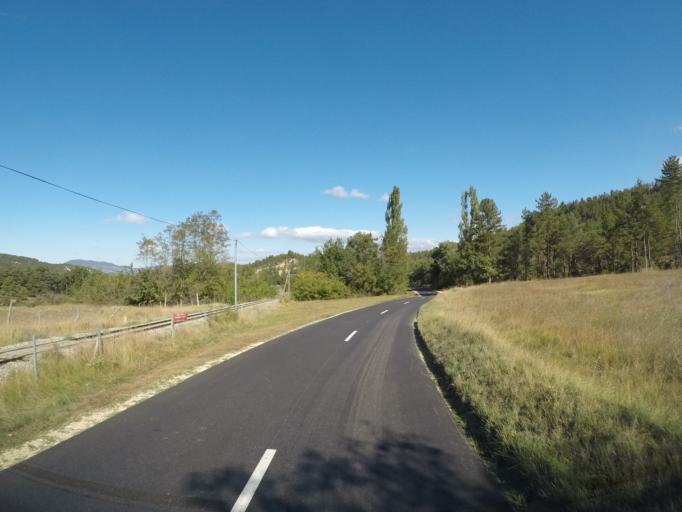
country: FR
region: Provence-Alpes-Cote d'Azur
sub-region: Departement des Alpes-de-Haute-Provence
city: Mallemoisson
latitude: 44.0176
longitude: 6.1789
